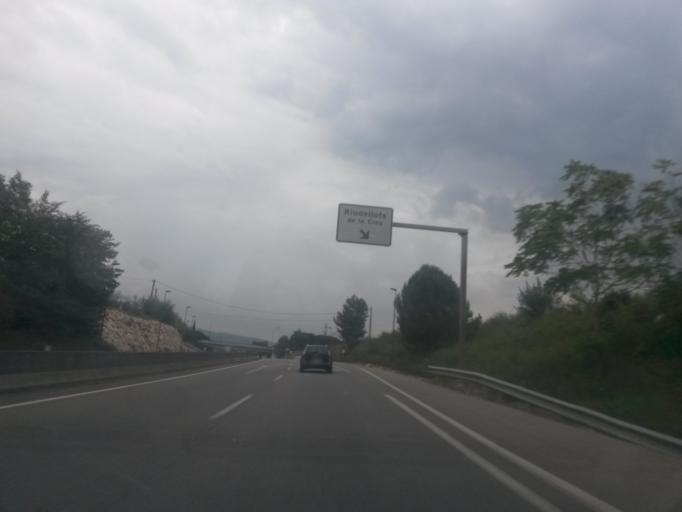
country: ES
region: Catalonia
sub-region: Provincia de Girona
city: Palol de Revardit
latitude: 42.0600
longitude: 2.8130
